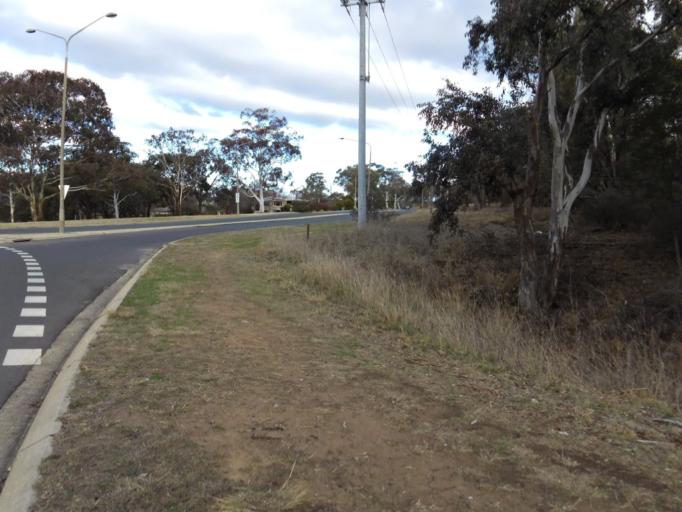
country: AU
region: Australian Capital Territory
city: Acton
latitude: -35.2588
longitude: 149.1097
